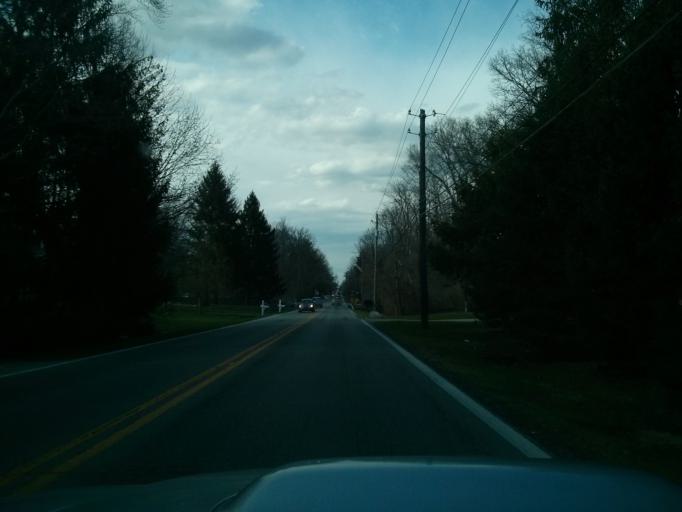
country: US
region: Indiana
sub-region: Marion County
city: Meridian Hills
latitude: 39.9032
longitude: -86.1457
